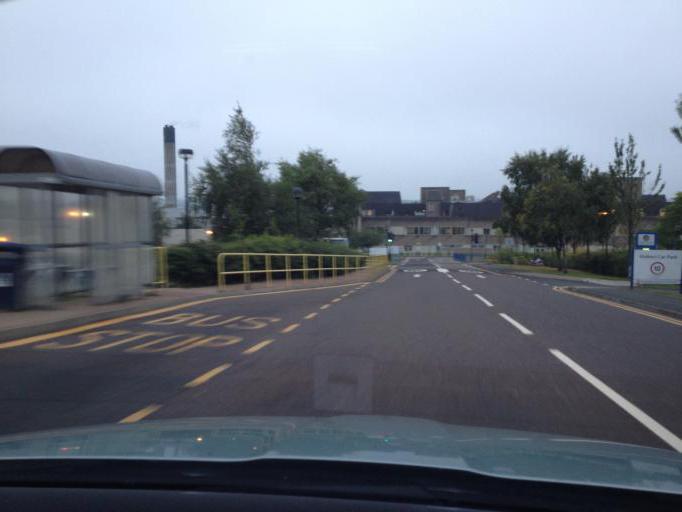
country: GB
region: Scotland
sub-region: West Lothian
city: Livingston
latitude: 55.8937
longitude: -3.5215
